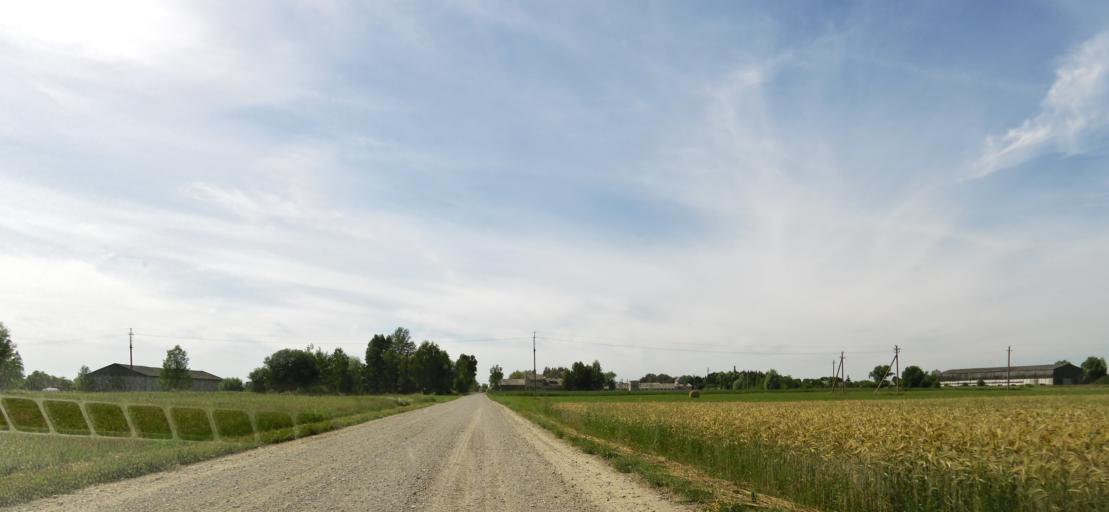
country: LT
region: Panevezys
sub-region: Panevezys City
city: Panevezys
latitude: 55.8842
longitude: 24.2881
